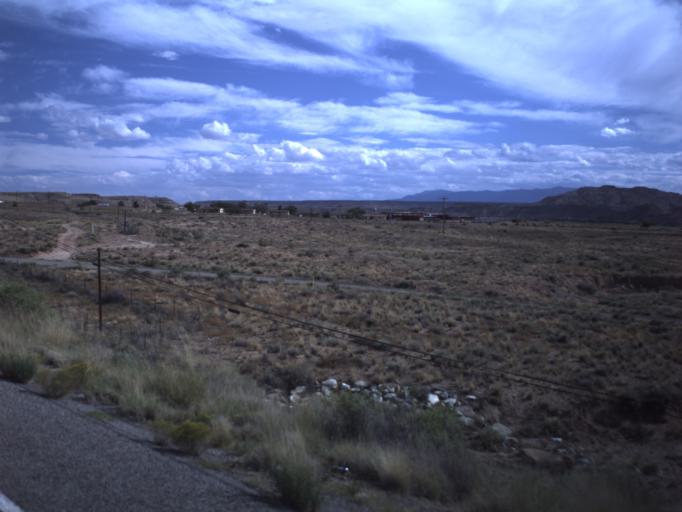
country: US
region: Colorado
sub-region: Montezuma County
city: Towaoc
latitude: 37.2034
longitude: -109.1590
